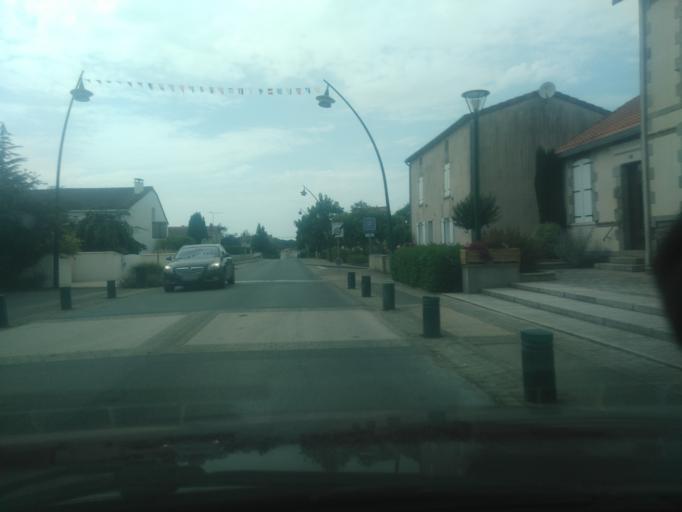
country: FR
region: Poitou-Charentes
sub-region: Departement des Deux-Sevres
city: Secondigny
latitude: 46.6344
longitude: -0.5113
